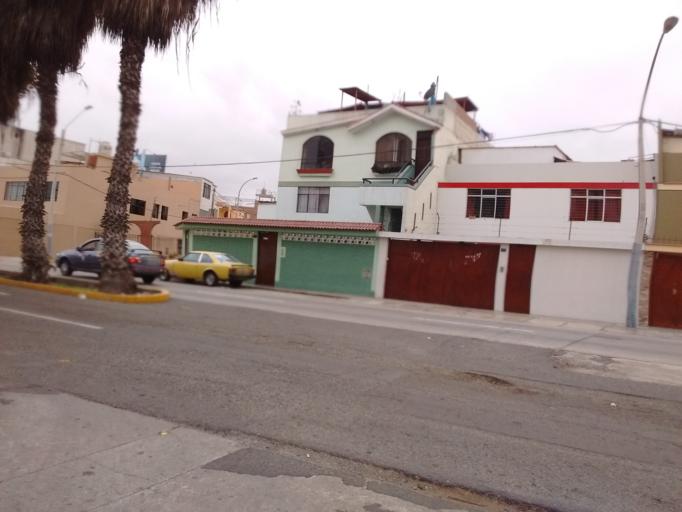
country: PE
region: Callao
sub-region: Callao
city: Callao
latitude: -12.0651
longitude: -77.0965
